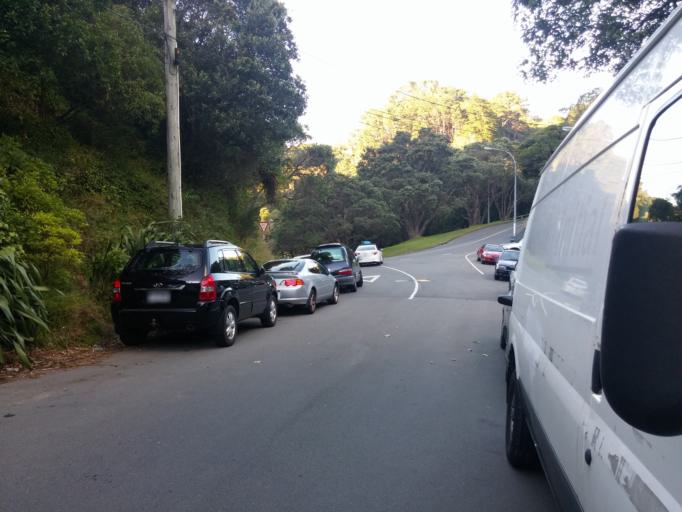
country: NZ
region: Wellington
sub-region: Wellington City
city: Kelburn
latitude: -41.2923
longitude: 174.7607
